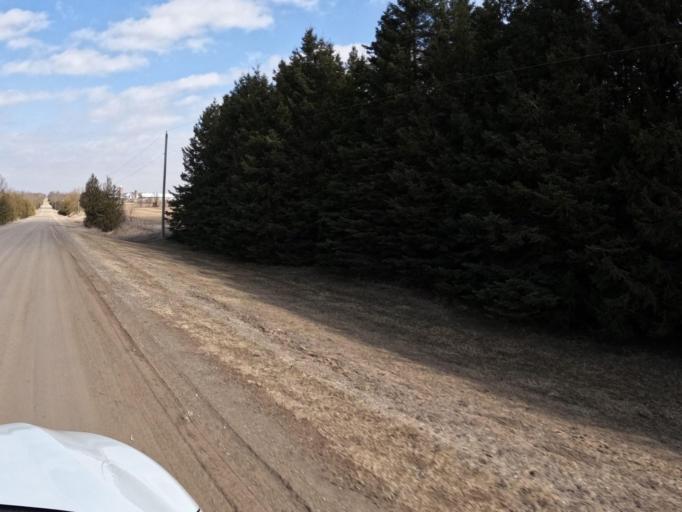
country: CA
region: Ontario
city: Orangeville
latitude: 43.9162
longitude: -80.2544
